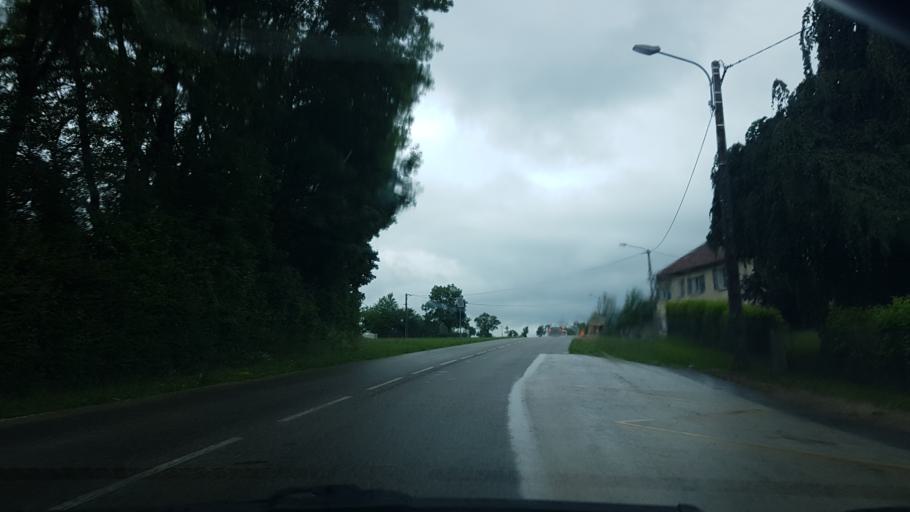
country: FR
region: Franche-Comte
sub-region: Departement du Jura
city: Clairvaux-les-Lacs
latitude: 46.5869
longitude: 5.7050
